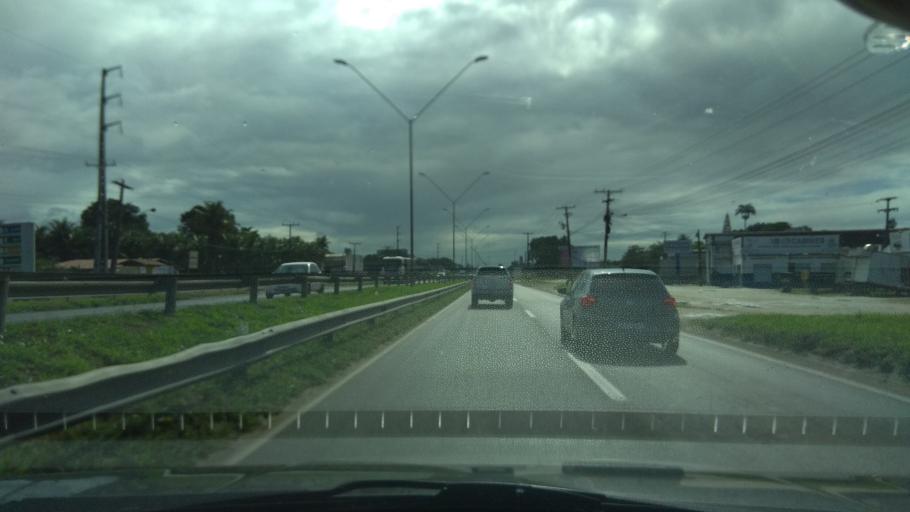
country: BR
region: Bahia
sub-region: Feira De Santana
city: Feira de Santana
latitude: -12.3090
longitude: -38.8869
